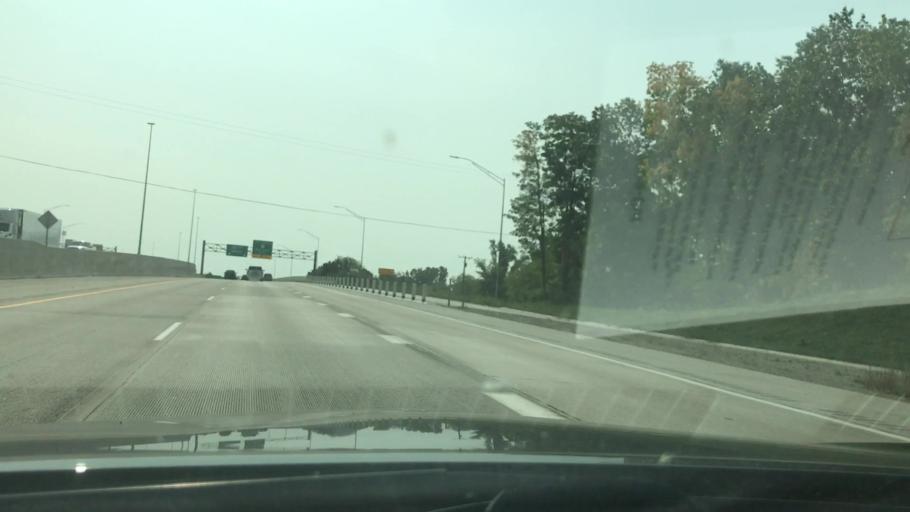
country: US
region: Michigan
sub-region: Livingston County
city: Brighton
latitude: 42.5294
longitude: -83.7643
